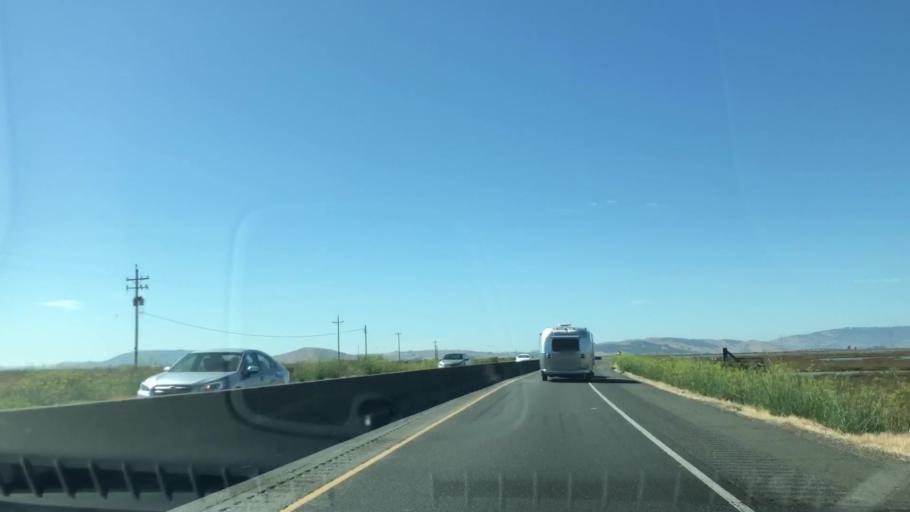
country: US
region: California
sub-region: Napa County
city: American Canyon
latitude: 38.1369
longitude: -122.3506
